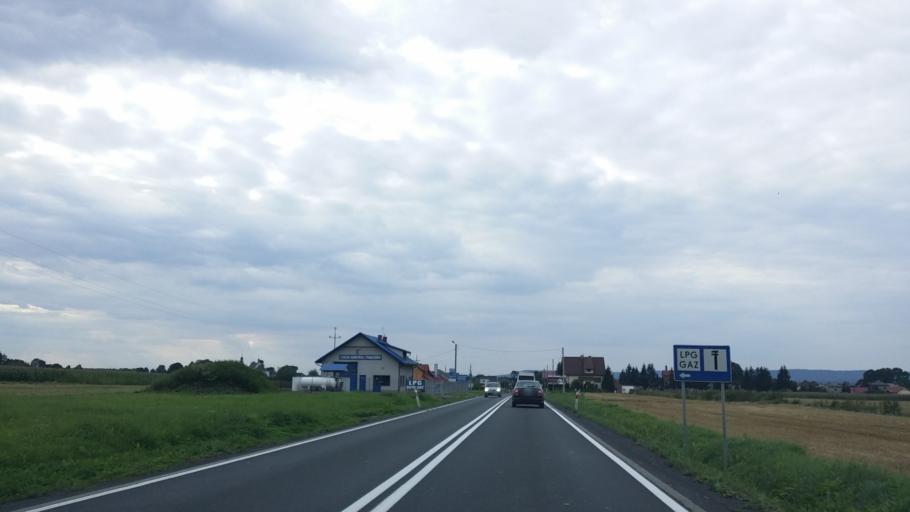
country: PL
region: Lesser Poland Voivodeship
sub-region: Powiat wadowicki
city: Spytkowice
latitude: 49.9917
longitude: 19.5193
